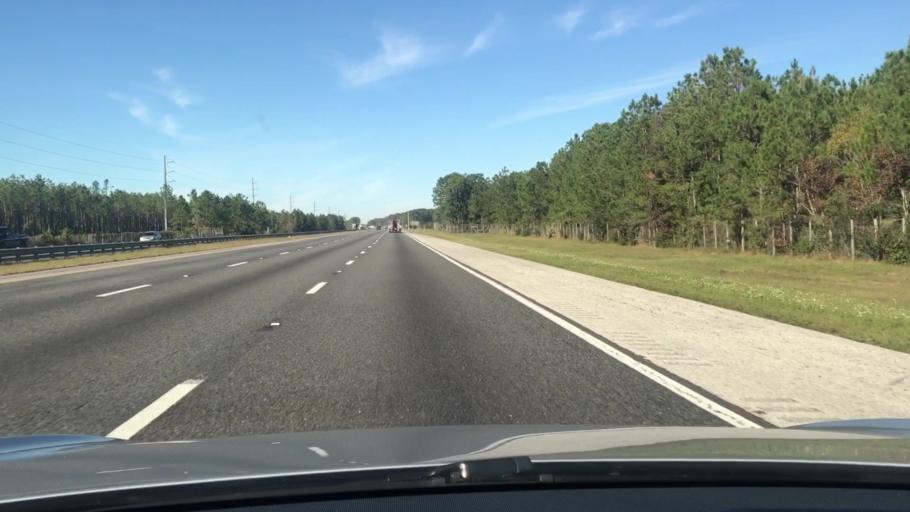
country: US
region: Florida
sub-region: Saint Johns County
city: Saint Augustine Shores
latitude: 29.7983
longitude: -81.3682
